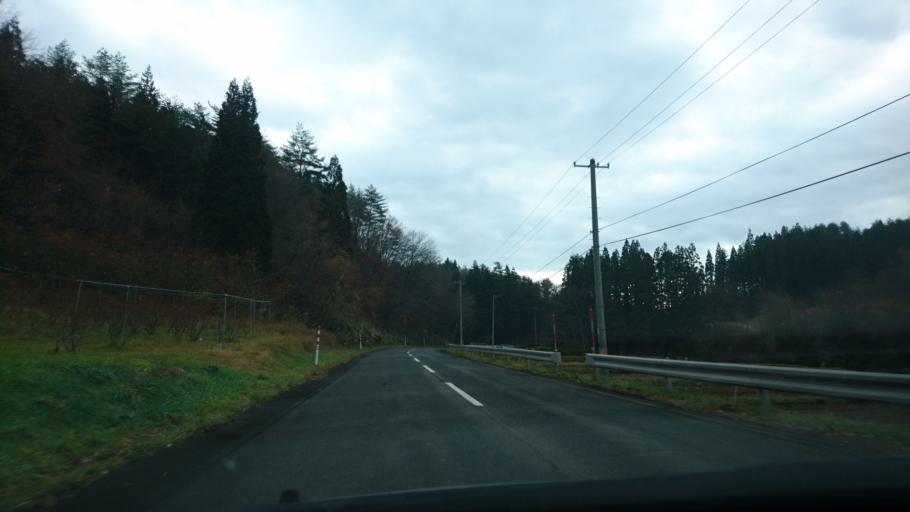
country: JP
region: Iwate
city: Ichinoseki
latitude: 38.9321
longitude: 140.9219
